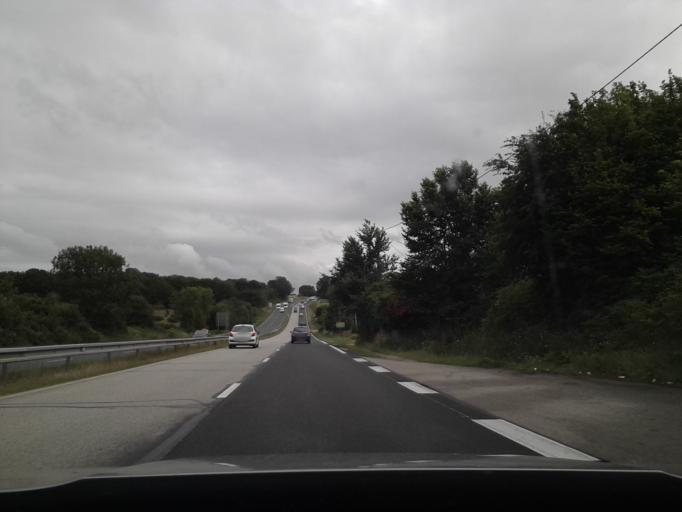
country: FR
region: Lower Normandy
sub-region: Departement de la Manche
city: Brix
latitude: 49.5568
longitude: -1.5645
